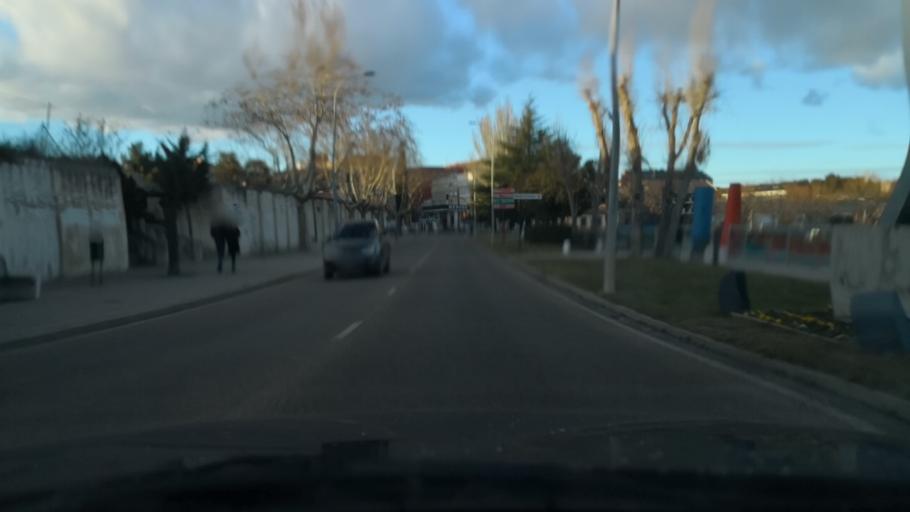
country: ES
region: Castille and Leon
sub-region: Provincia de Valladolid
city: Medina del Campo
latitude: 41.3036
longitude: -4.9102
